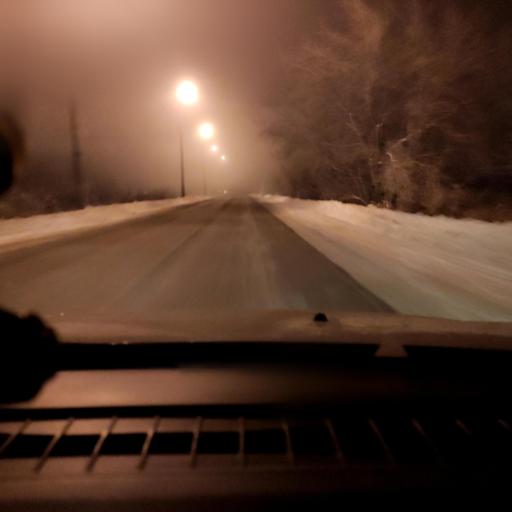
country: RU
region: Samara
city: Samara
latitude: 53.1322
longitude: 50.1499
